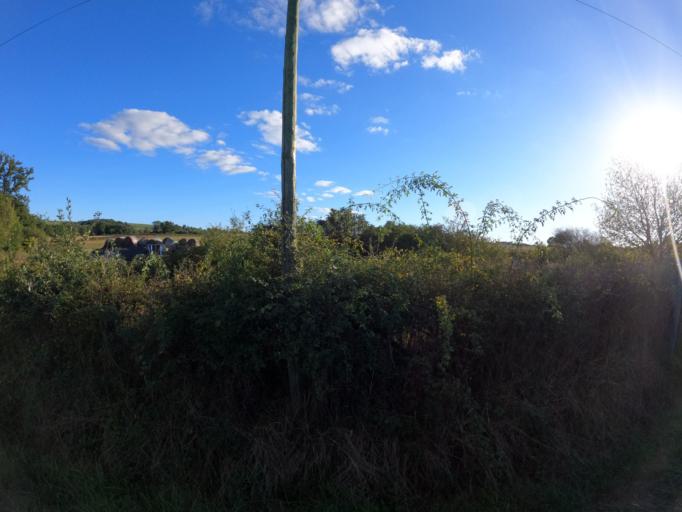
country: FR
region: Bourgogne
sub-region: Departement de Saone-et-Loire
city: Saint-Leu
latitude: 46.7534
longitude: 4.5106
